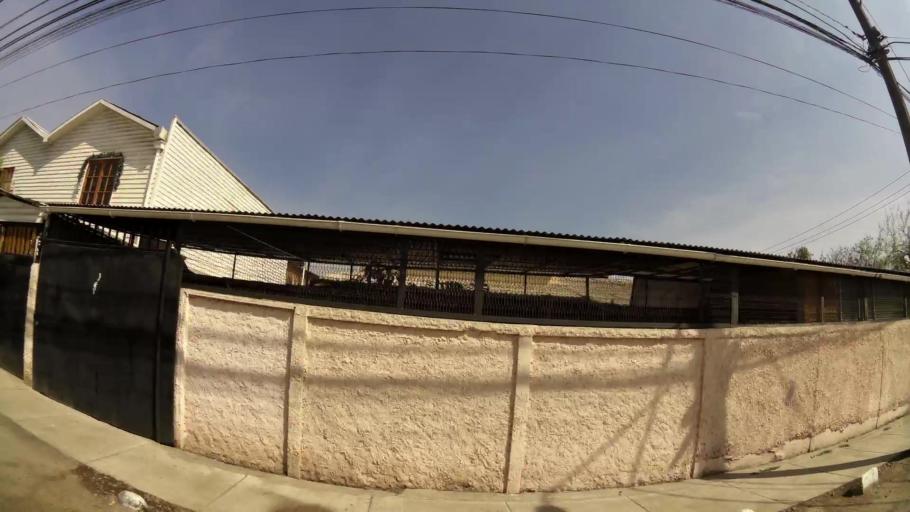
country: CL
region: Santiago Metropolitan
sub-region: Provincia de Santiago
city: Villa Presidente Frei, Nunoa, Santiago, Chile
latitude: -33.5139
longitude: -70.5829
